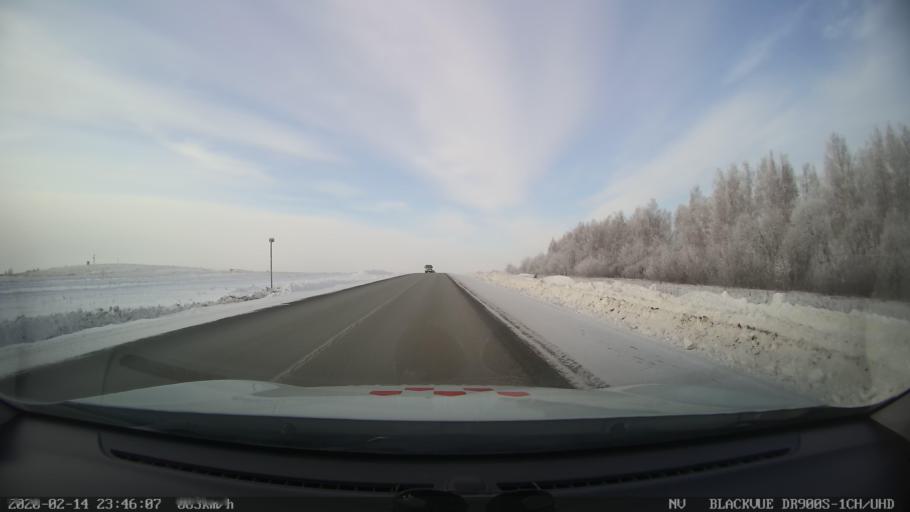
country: RU
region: Tatarstan
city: Kuybyshevskiy Zaton
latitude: 55.2281
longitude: 49.2294
